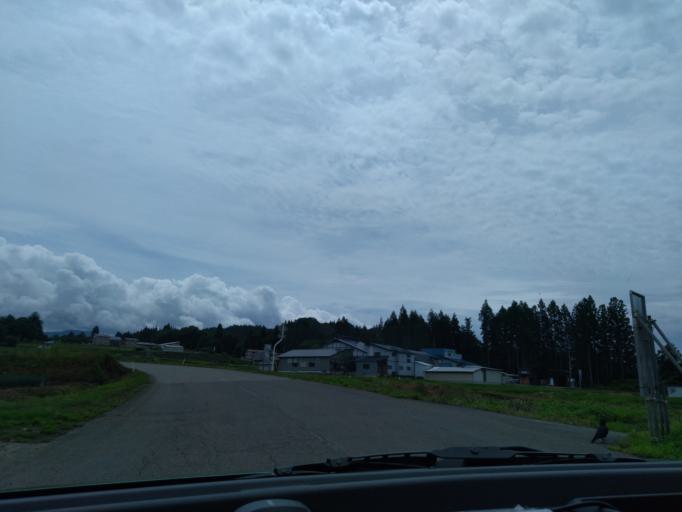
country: JP
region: Akita
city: Kakunodatemachi
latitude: 39.5829
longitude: 140.6240
